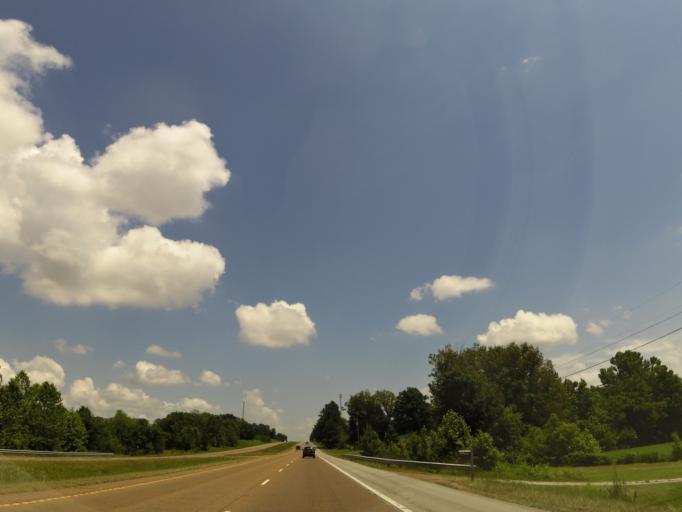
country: US
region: Tennessee
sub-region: Lauderdale County
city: Halls
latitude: 35.9150
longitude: -89.2695
